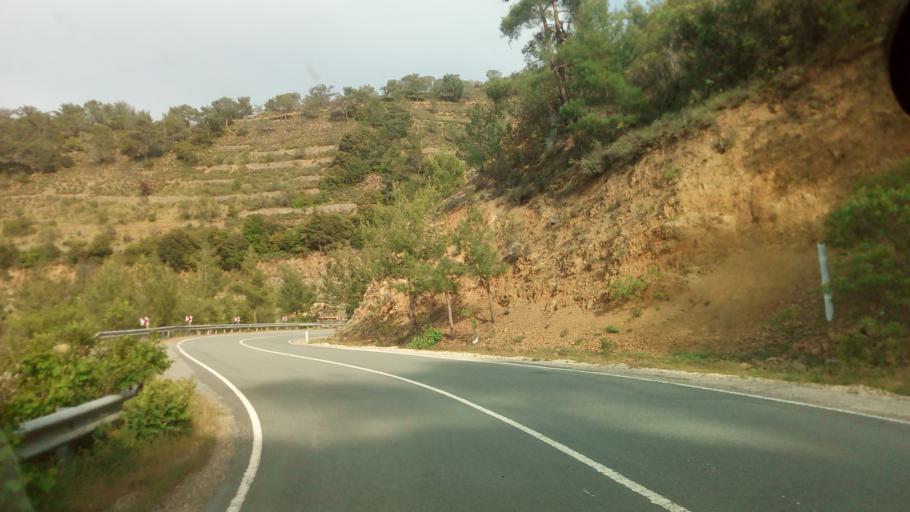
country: CY
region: Lefkosia
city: Kakopetria
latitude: 35.0003
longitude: 32.7956
